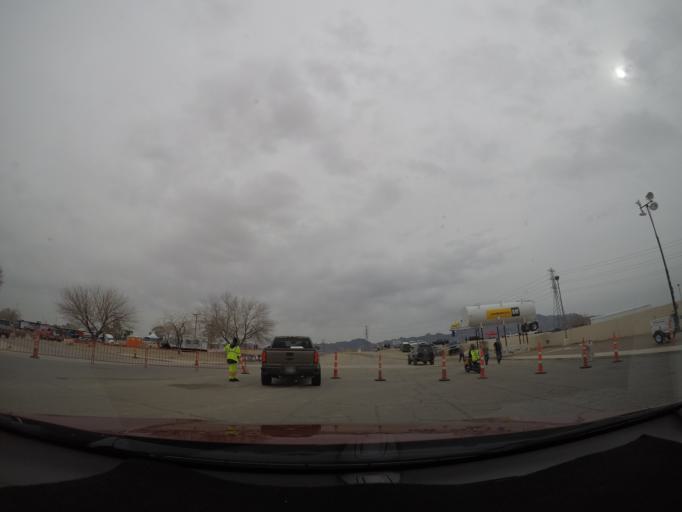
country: US
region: Nevada
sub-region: Clark County
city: Sandy Valley
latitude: 35.6135
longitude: -115.3807
